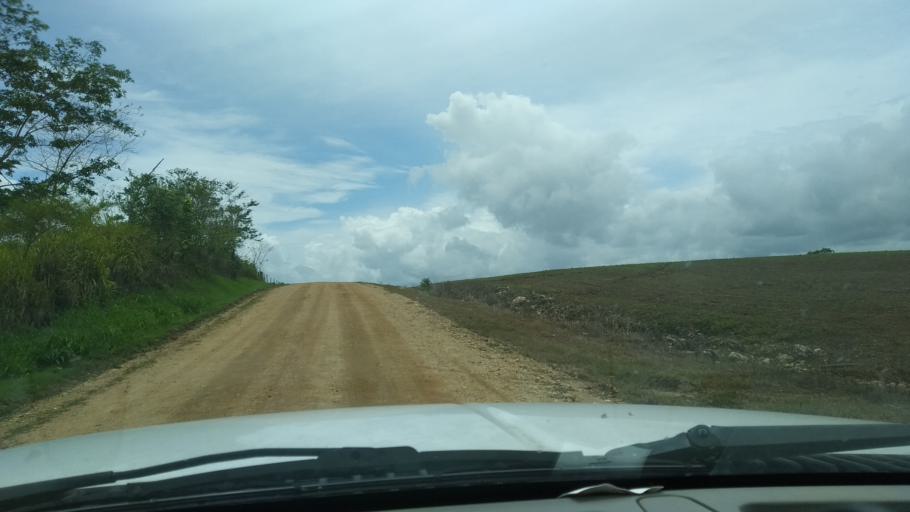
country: BZ
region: Cayo
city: San Ignacio
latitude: 17.2263
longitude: -88.9745
